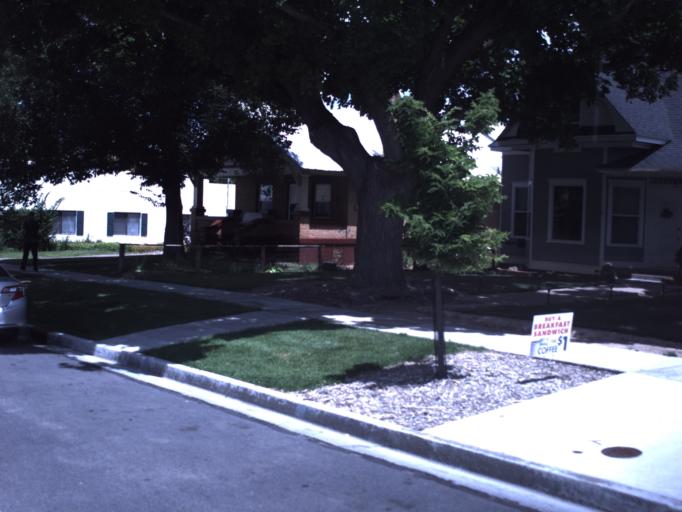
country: US
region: Utah
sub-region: Iron County
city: Parowan
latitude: 37.8428
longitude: -112.8276
